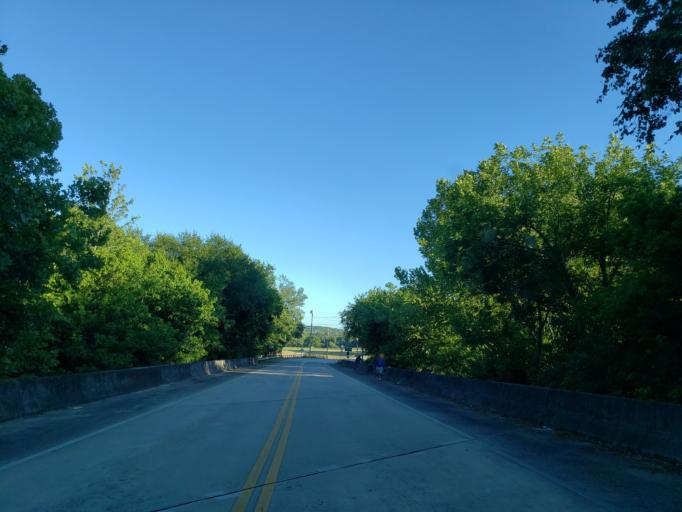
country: US
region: Georgia
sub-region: Bartow County
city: Euharlee
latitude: 34.0961
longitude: -84.9913
